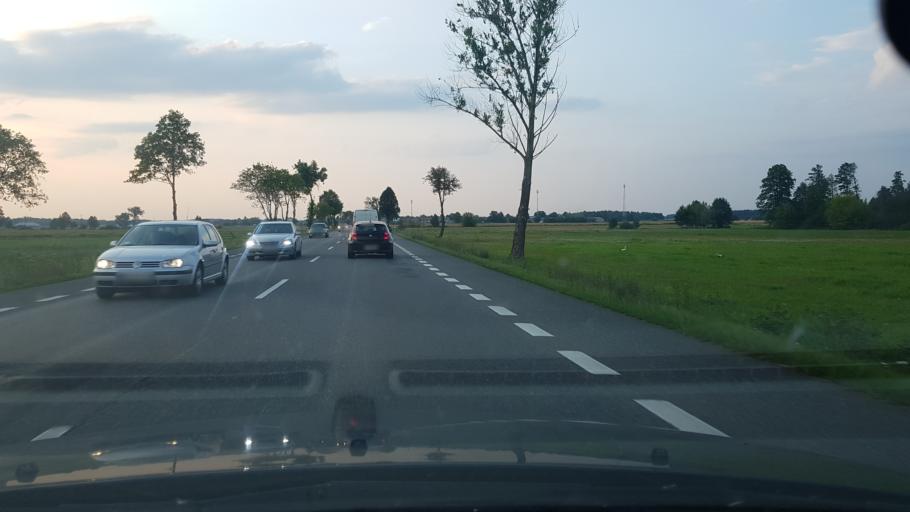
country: PL
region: Masovian Voivodeship
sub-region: Powiat mlawski
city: Strzegowo
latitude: 52.9326
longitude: 20.2850
